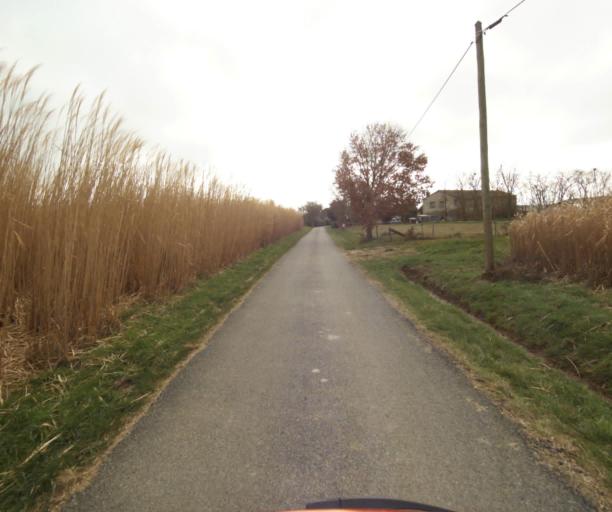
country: FR
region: Midi-Pyrenees
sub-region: Departement de l'Ariege
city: Mazeres
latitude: 43.1960
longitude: 1.6708
